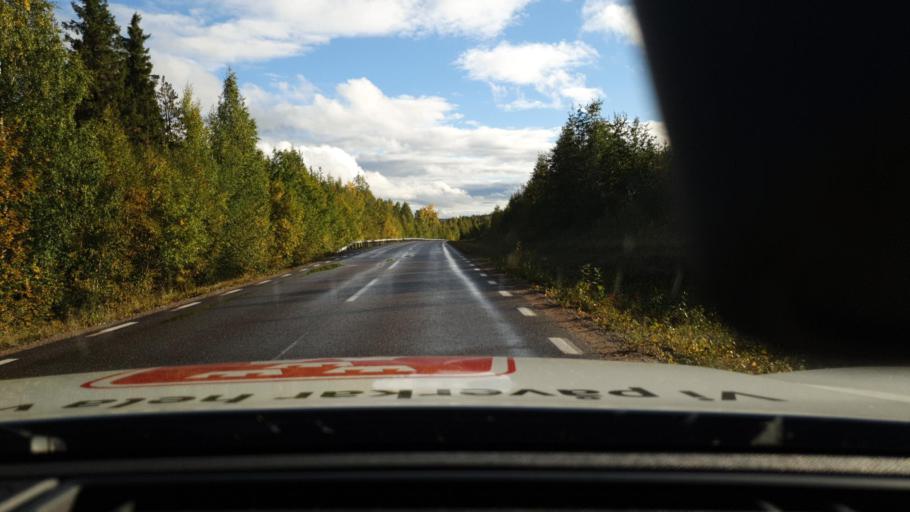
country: SE
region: Norrbotten
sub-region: Overkalix Kommun
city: OEverkalix
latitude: 66.7518
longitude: 22.6723
